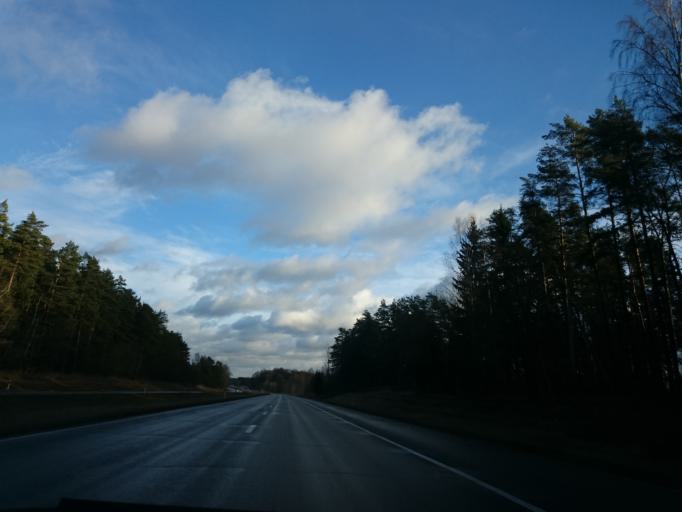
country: LV
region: Incukalns
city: Incukalns
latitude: 57.1221
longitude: 24.6719
